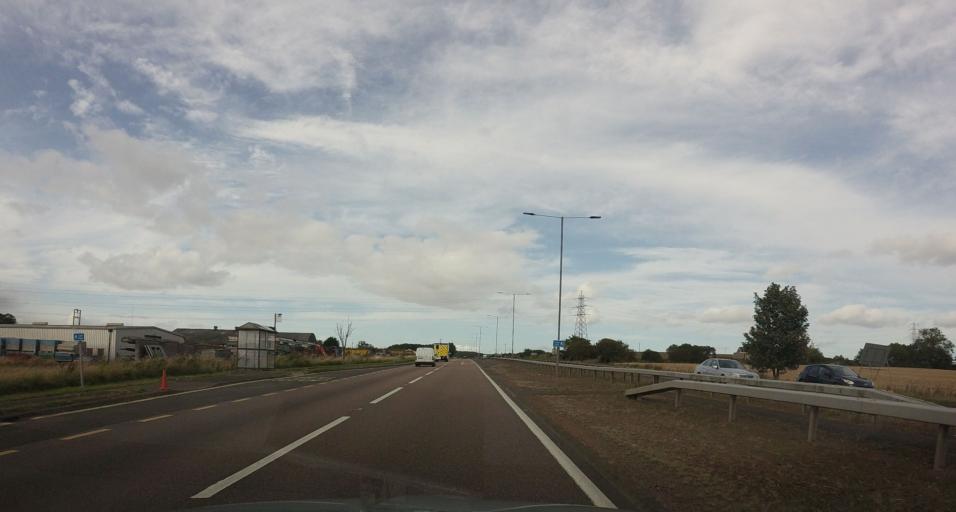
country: GB
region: Scotland
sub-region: Dundee City
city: Dundee
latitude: 56.5183
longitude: -2.9450
